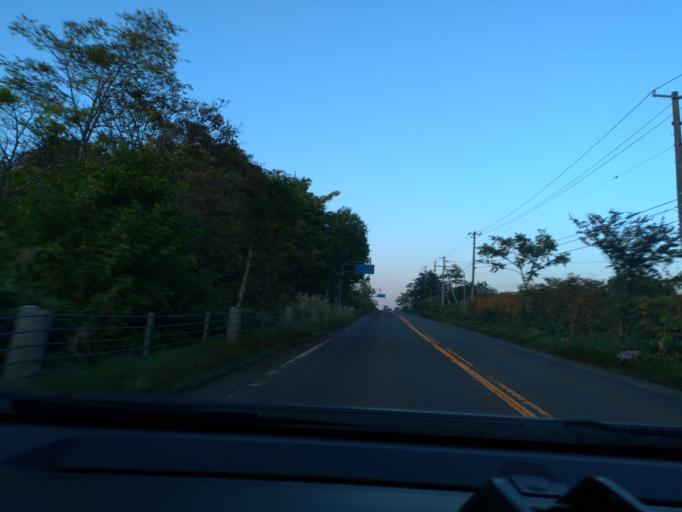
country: JP
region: Hokkaido
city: Tobetsu
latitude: 43.3165
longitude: 141.6024
